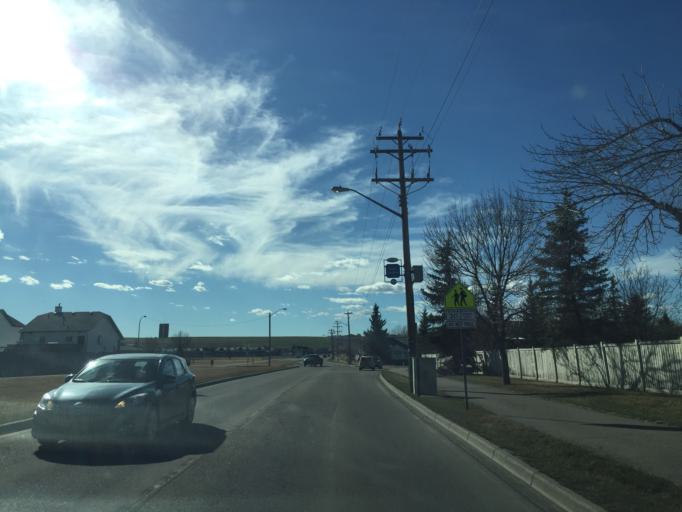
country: CA
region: Alberta
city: Airdrie
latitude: 51.2928
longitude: -114.0320
